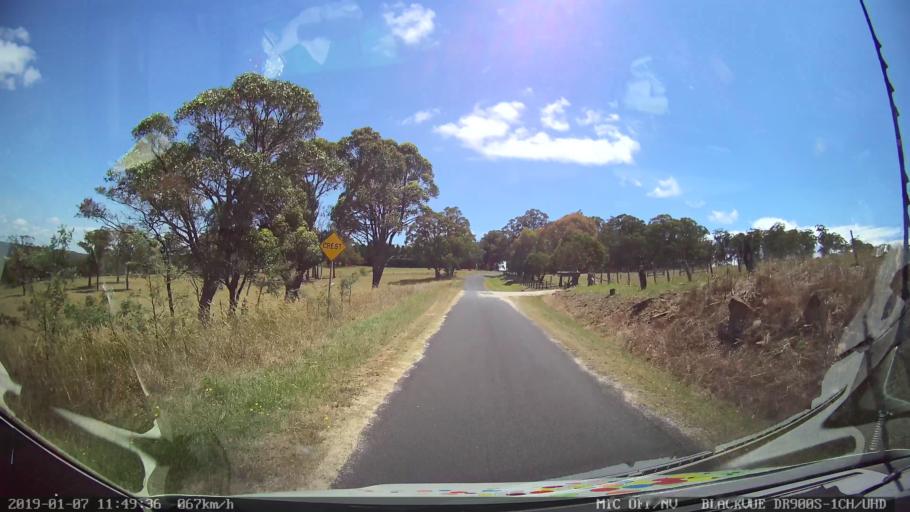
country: AU
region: New South Wales
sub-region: Guyra
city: Guyra
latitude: -30.3173
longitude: 151.6292
